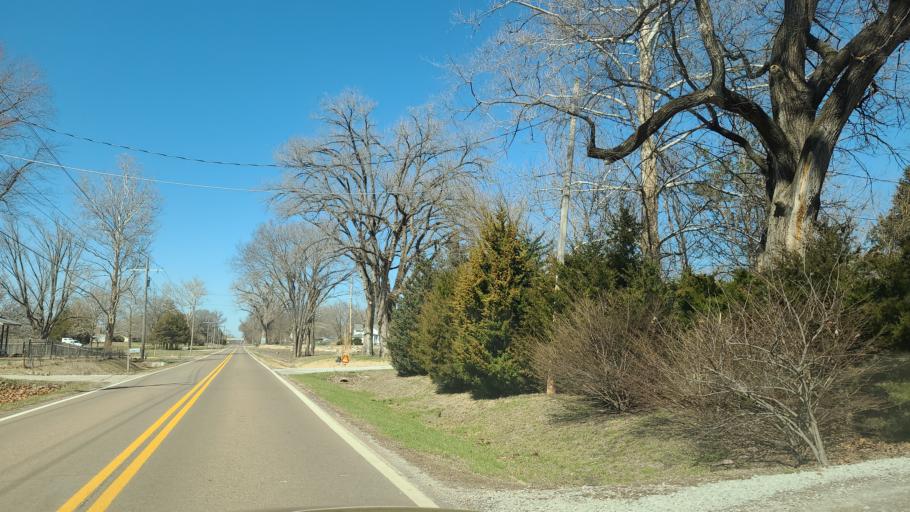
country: US
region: Kansas
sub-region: Douglas County
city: Lawrence
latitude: 38.9872
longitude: -95.2239
